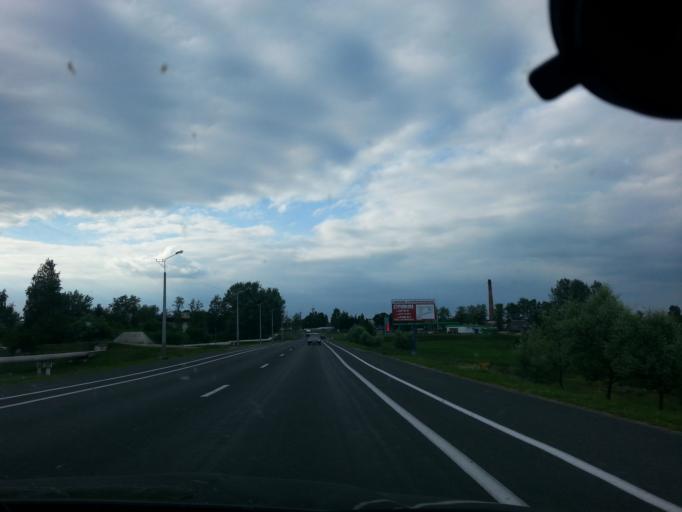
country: BY
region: Minsk
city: Myadzyel
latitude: 54.8805
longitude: 26.9397
